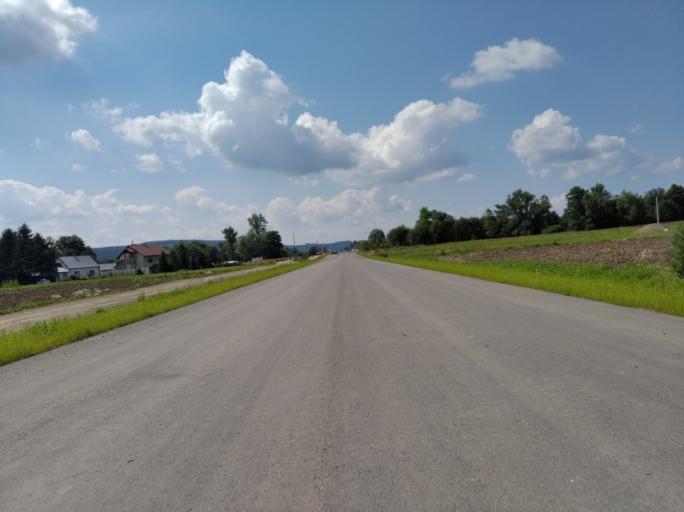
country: PL
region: Subcarpathian Voivodeship
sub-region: Powiat rzeszowski
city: Dynow
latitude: 49.8292
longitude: 22.2416
